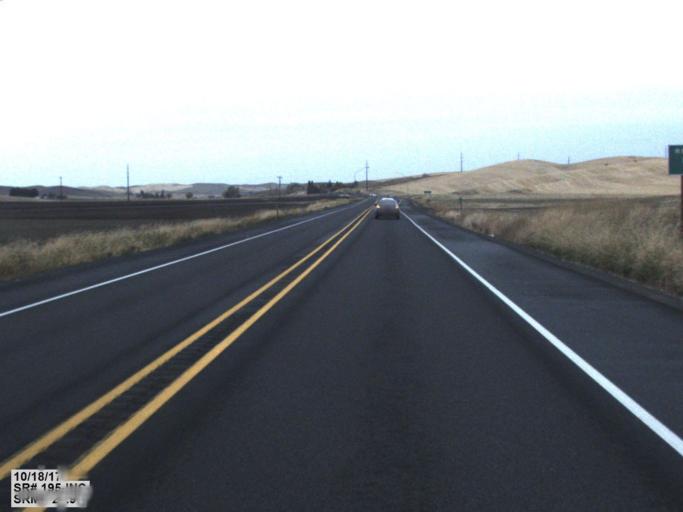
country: US
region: Washington
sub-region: Whitman County
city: Pullman
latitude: 46.7673
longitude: -117.2694
